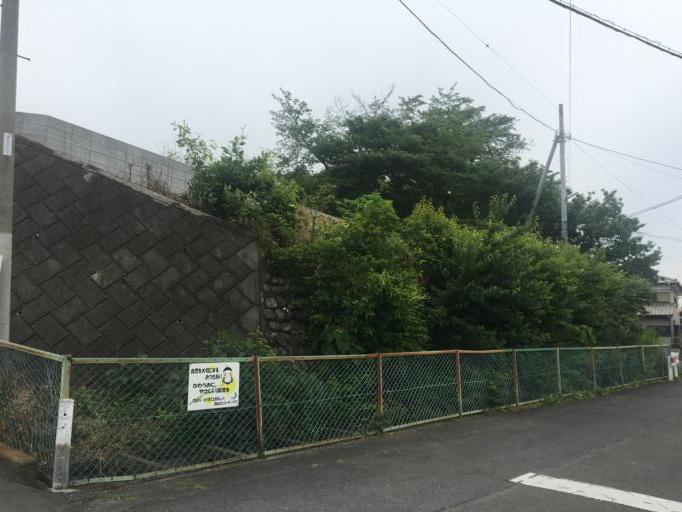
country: JP
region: Saitama
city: Sakado
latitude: 36.0316
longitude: 139.4112
